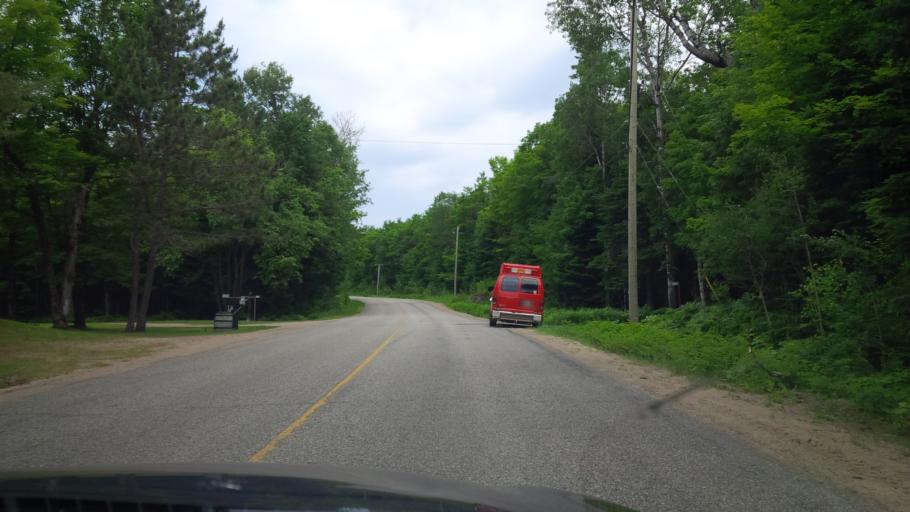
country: CA
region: Ontario
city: Huntsville
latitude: 45.6267
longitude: -79.1523
